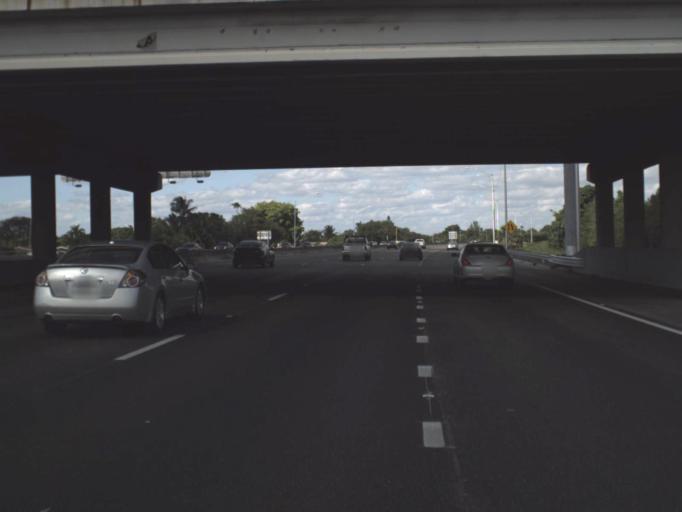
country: US
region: Florida
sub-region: Broward County
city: Miramar
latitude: 25.9815
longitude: -80.2299
